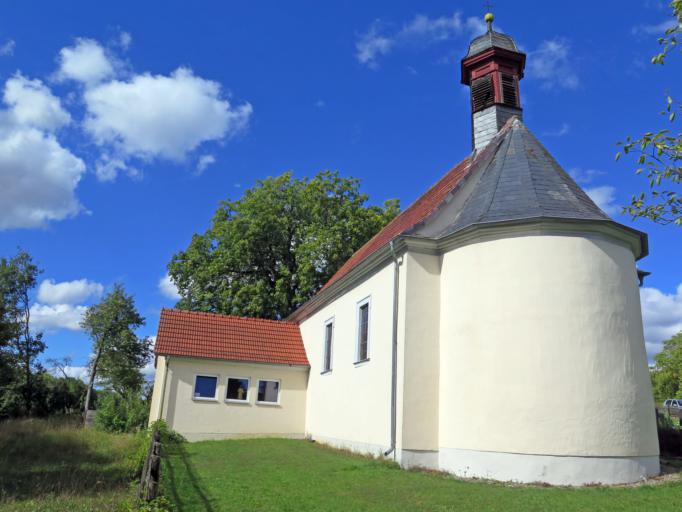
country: DE
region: Bavaria
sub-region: Regierungsbezirk Unterfranken
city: Wonfurt
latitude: 50.0588
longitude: 10.4492
